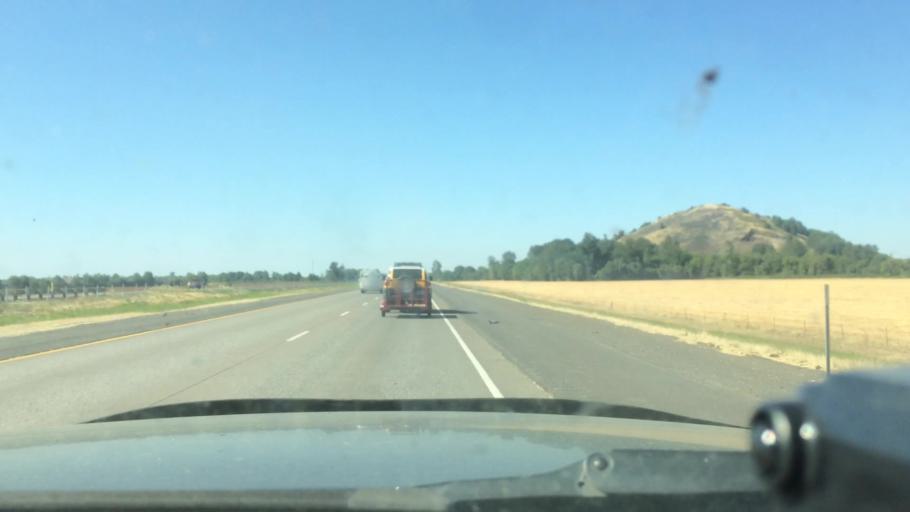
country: US
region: Oregon
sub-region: Linn County
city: Brownsville
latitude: 44.4440
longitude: -123.0613
